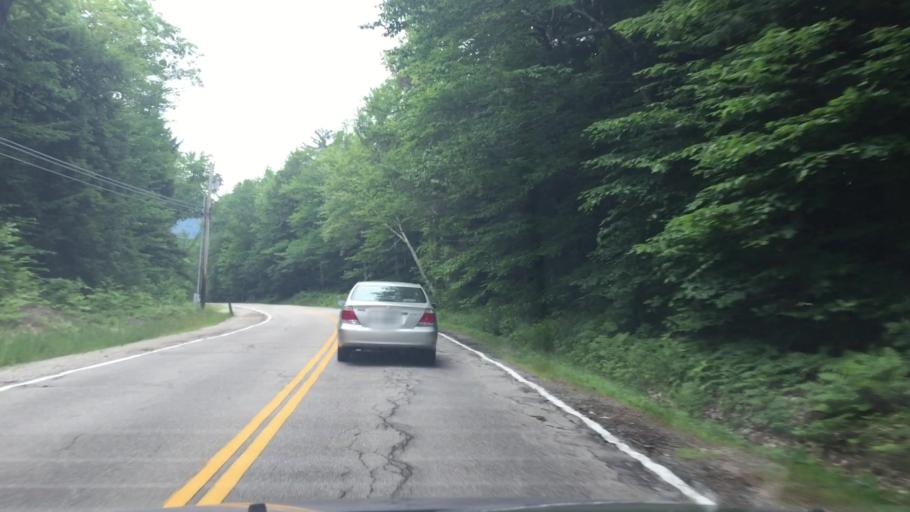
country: US
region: New Hampshire
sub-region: Carroll County
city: Conway
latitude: 43.9326
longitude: -71.0868
